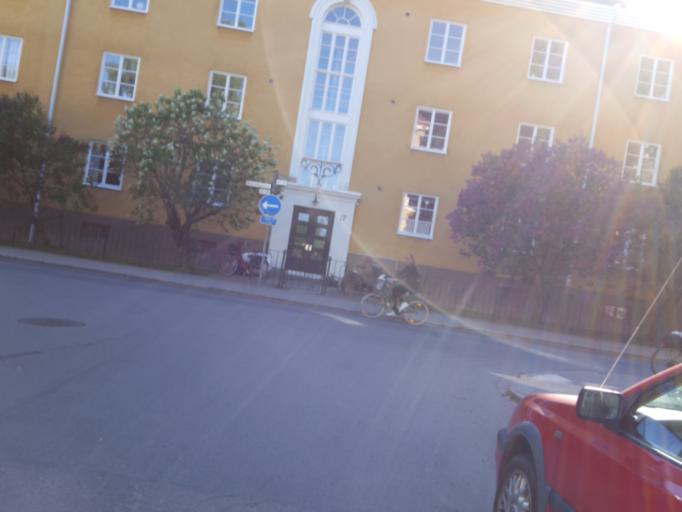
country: SE
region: Uppsala
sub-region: Uppsala Kommun
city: Uppsala
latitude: 59.8627
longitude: 17.6499
